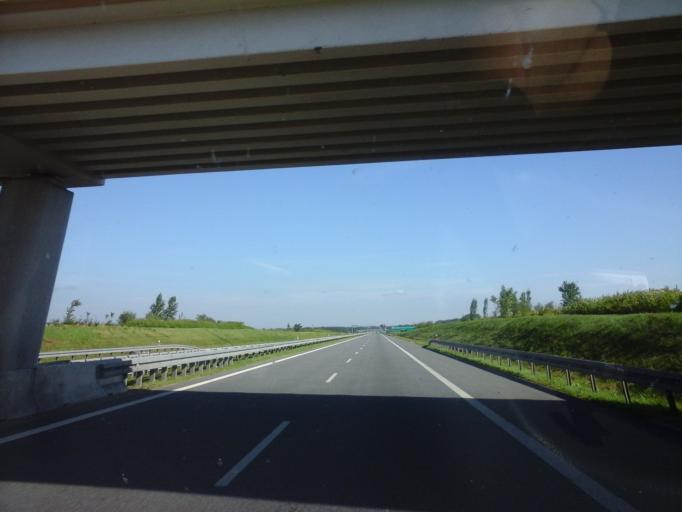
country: PL
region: West Pomeranian Voivodeship
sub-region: Powiat pyrzycki
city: Warnice
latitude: 53.3318
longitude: 14.9595
